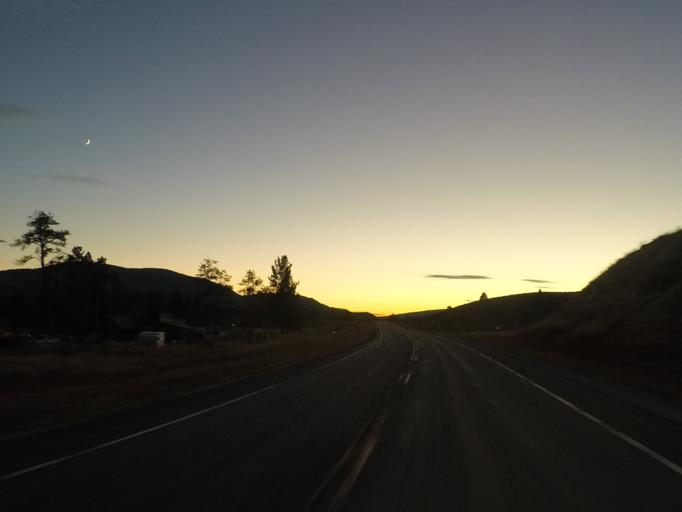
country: US
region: Montana
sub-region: Missoula County
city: Seeley Lake
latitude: 47.0429
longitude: -113.2138
